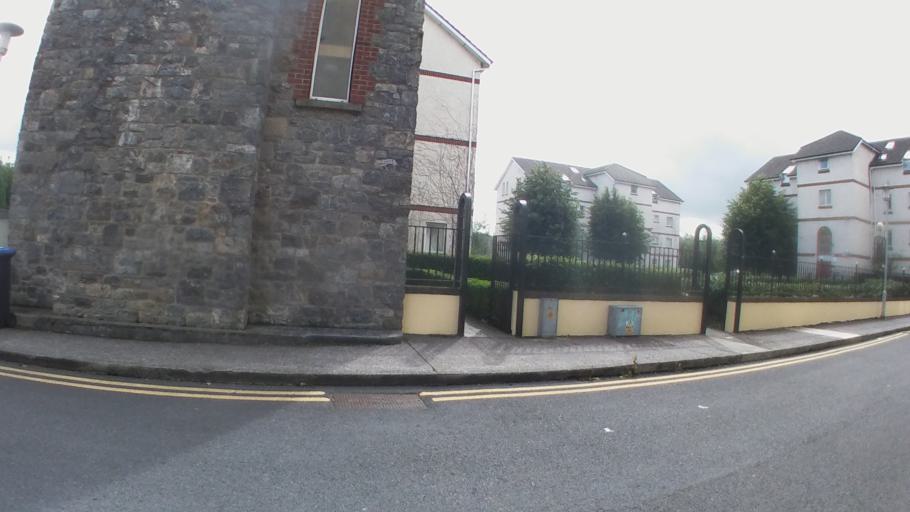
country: IE
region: Leinster
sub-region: County Carlow
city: Carlow
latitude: 52.8359
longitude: -6.9367
